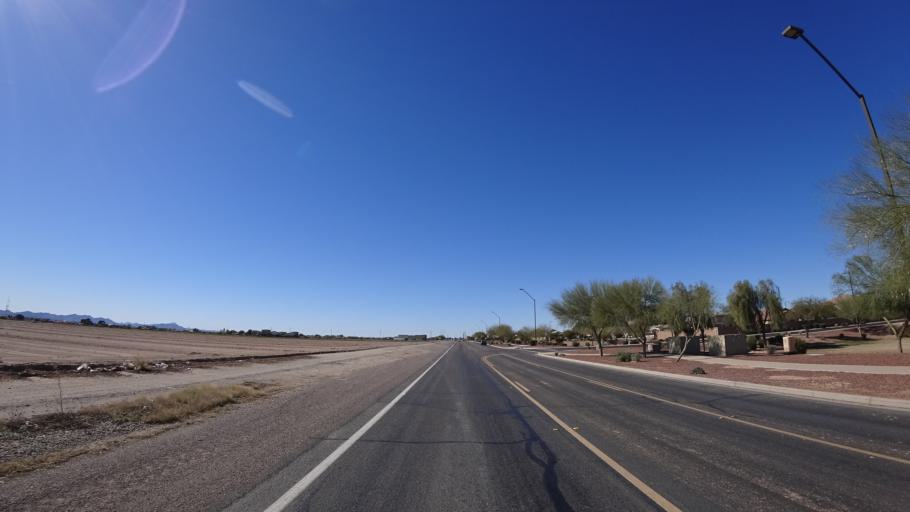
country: US
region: Arizona
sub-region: Maricopa County
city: Buckeye
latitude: 33.3921
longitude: -112.5841
